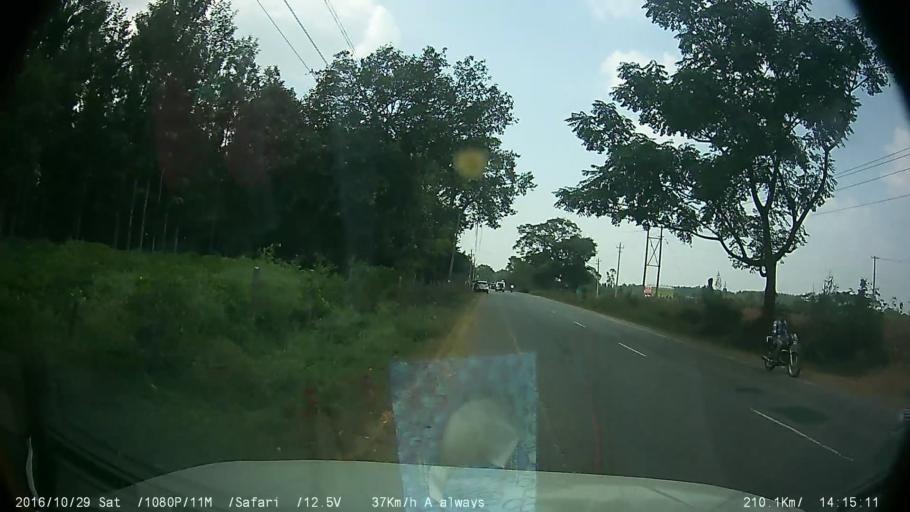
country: IN
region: Karnataka
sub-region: Mysore
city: Piriyapatna
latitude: 12.3830
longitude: 76.0319
